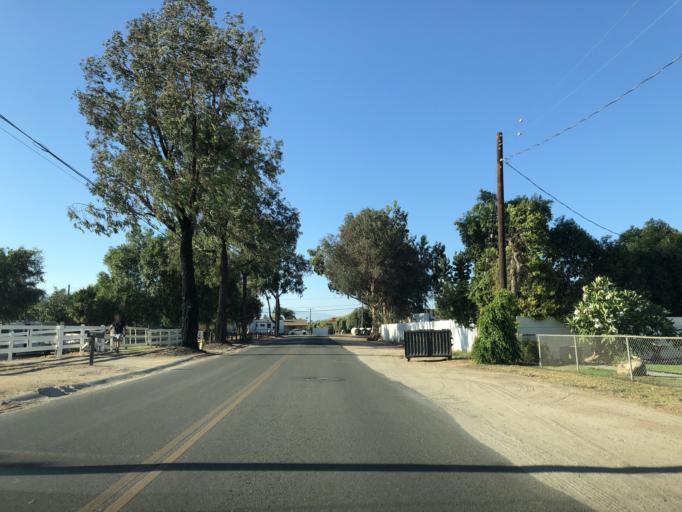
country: US
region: California
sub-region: Riverside County
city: Norco
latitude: 33.9156
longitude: -117.5440
